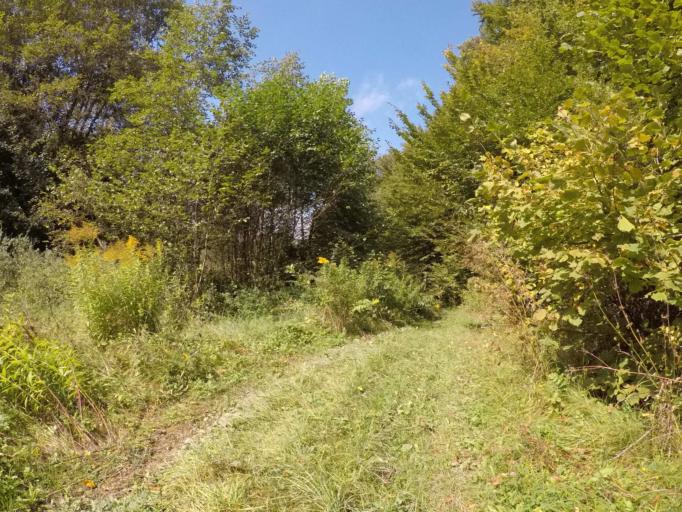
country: SK
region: Presovsky
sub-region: Okres Presov
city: Presov
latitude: 48.9334
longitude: 21.1636
